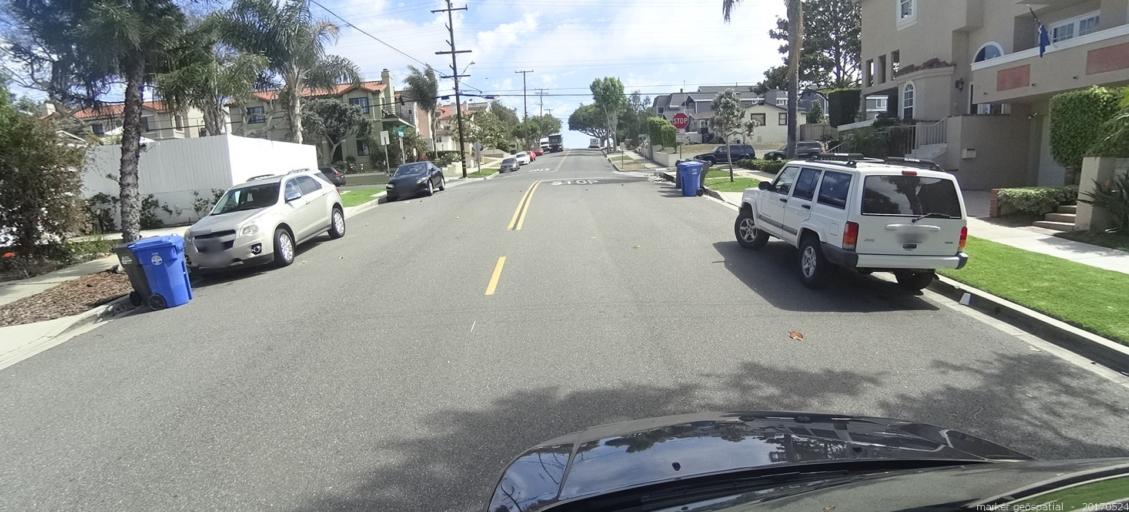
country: US
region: California
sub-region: Los Angeles County
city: Redondo Beach
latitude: 33.8410
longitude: -118.3789
